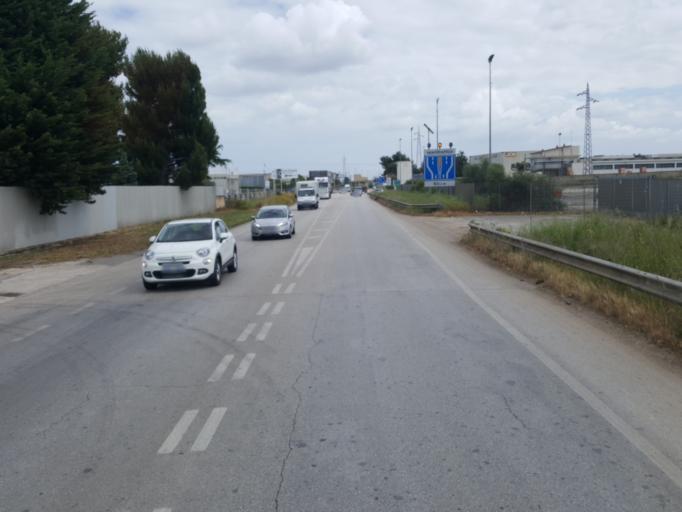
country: IT
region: Apulia
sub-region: Provincia di Bari
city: Modugno
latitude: 41.0937
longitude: 16.7499
